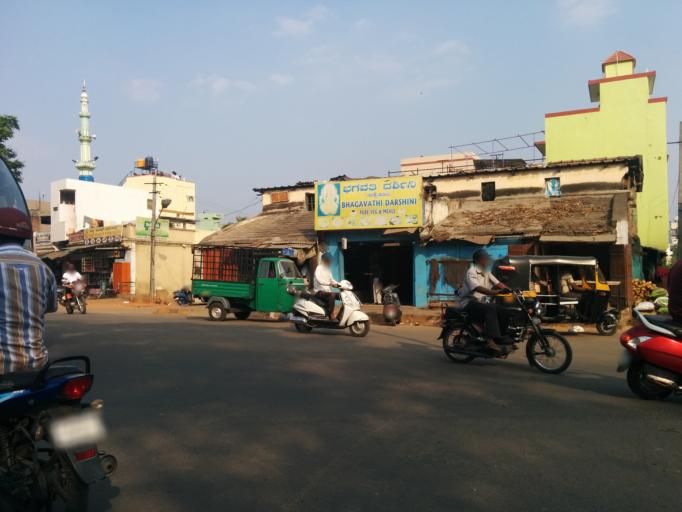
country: IN
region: Karnataka
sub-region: Mysore
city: Mysore
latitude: 12.2932
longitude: 76.6485
